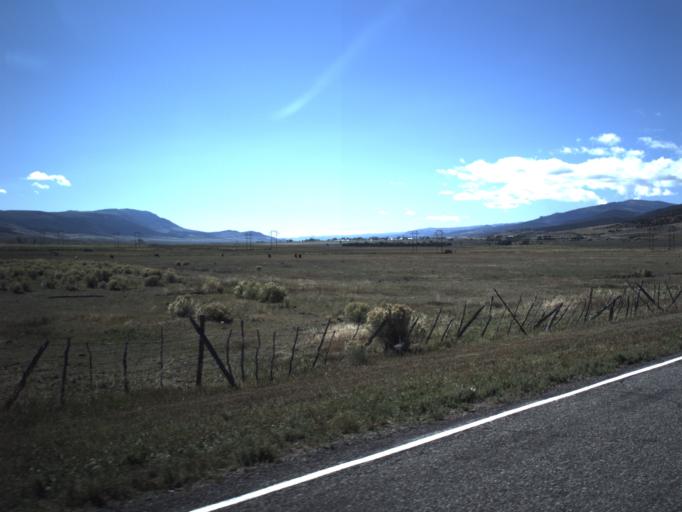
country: US
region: Utah
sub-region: Wayne County
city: Loa
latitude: 38.5606
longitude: -111.8558
